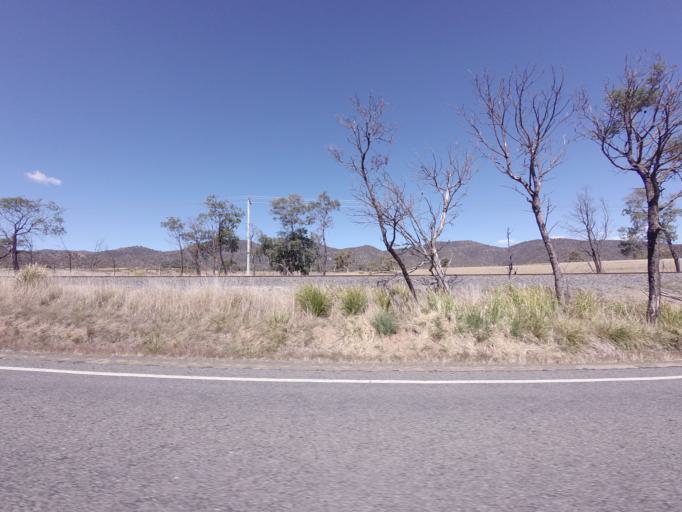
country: AU
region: Tasmania
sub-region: Northern Midlands
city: Evandale
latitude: -41.7414
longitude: 147.7922
